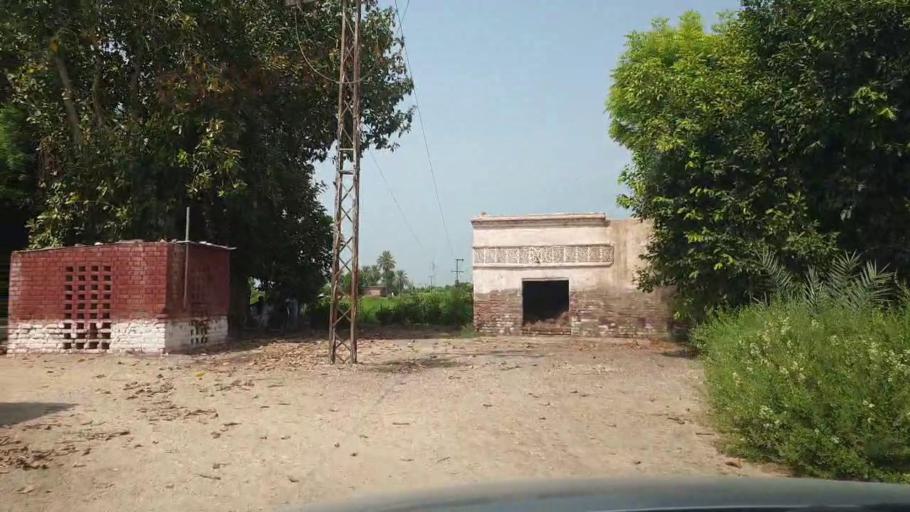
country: PK
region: Sindh
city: Madeji
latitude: 27.7858
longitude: 68.5369
